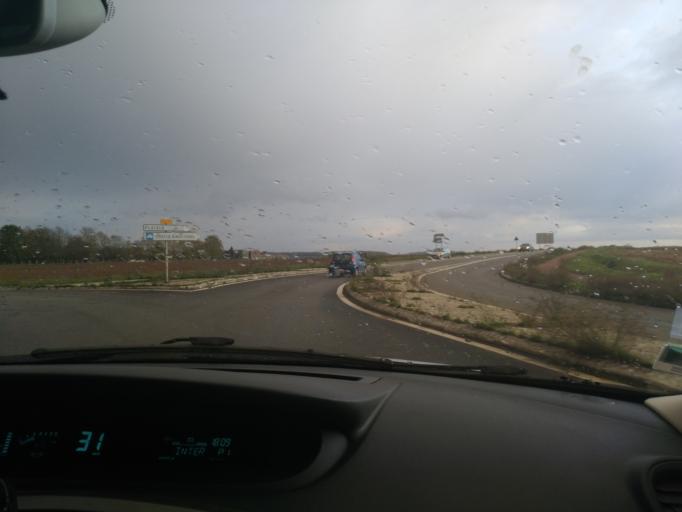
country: FR
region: Ile-de-France
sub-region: Departement des Yvelines
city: Plaisir
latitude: 48.8424
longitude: 1.9442
